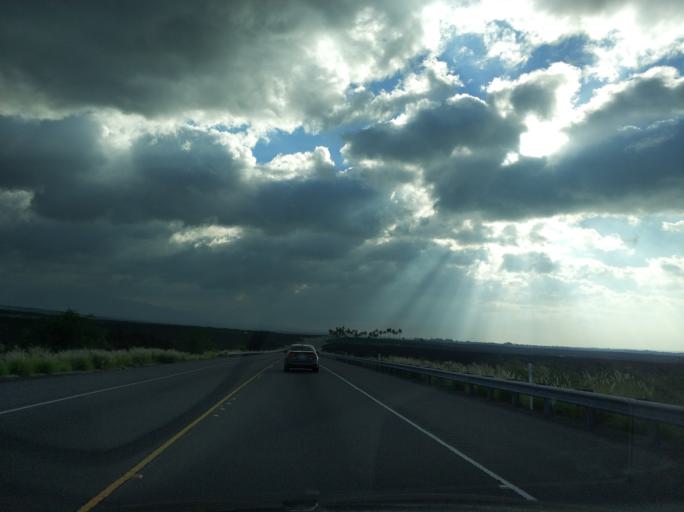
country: US
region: Hawaii
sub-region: Hawaii County
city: Waikoloa Village
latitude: 19.9397
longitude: -155.8384
